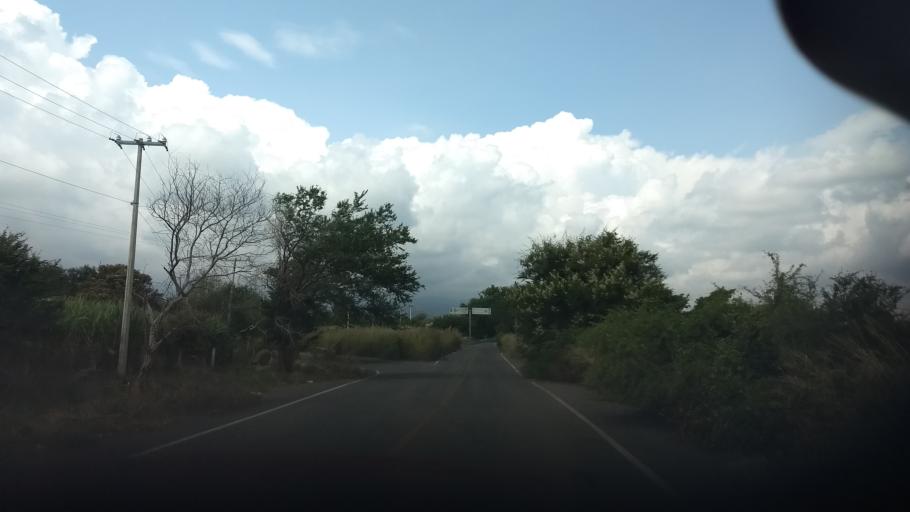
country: MX
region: Jalisco
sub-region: Tonila
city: San Marcos
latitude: 19.4323
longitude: -103.4931
